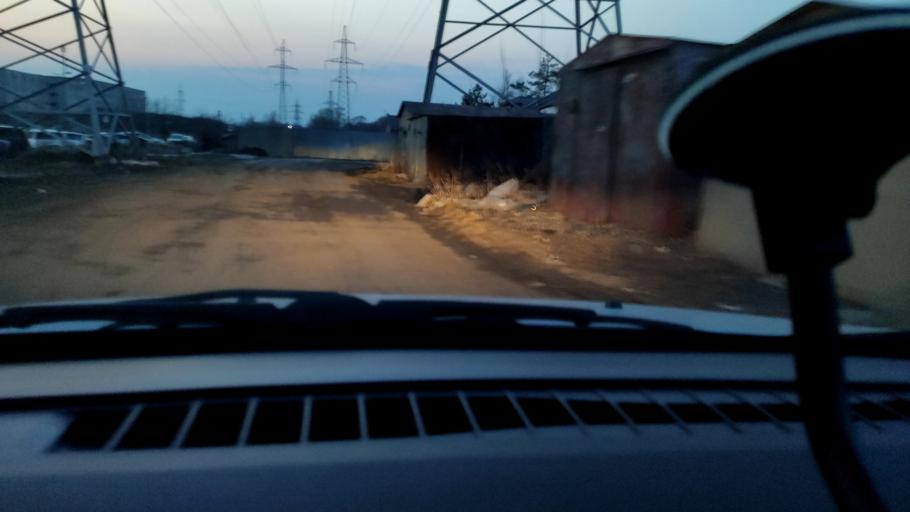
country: RU
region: Samara
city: Samara
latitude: 53.2666
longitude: 50.2333
